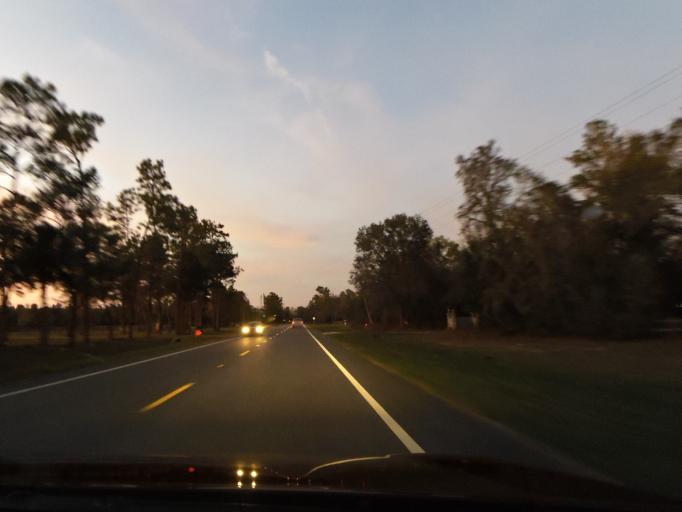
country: US
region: Florida
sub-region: Volusia County
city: De Leon Springs
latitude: 29.2122
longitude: -81.3151
